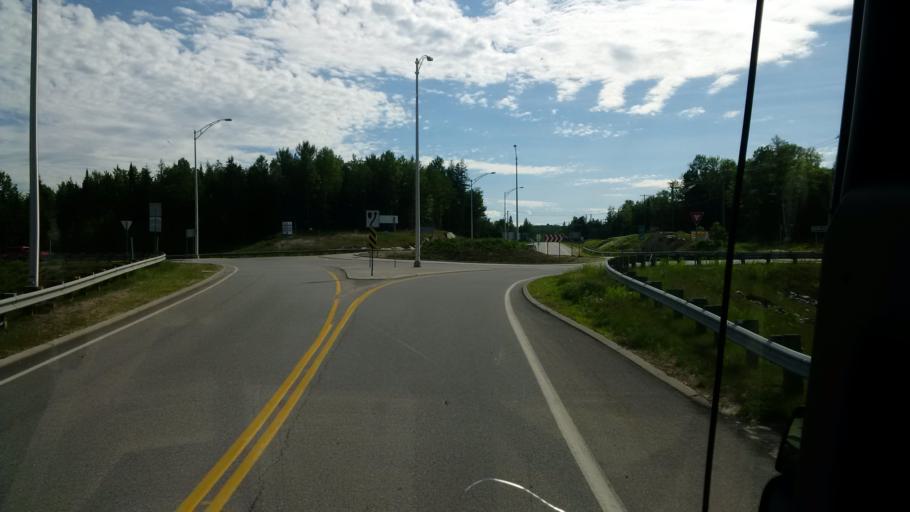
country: CA
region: Quebec
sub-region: Laurentides
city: Riviere-Rouge
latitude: 46.4335
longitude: -74.9023
